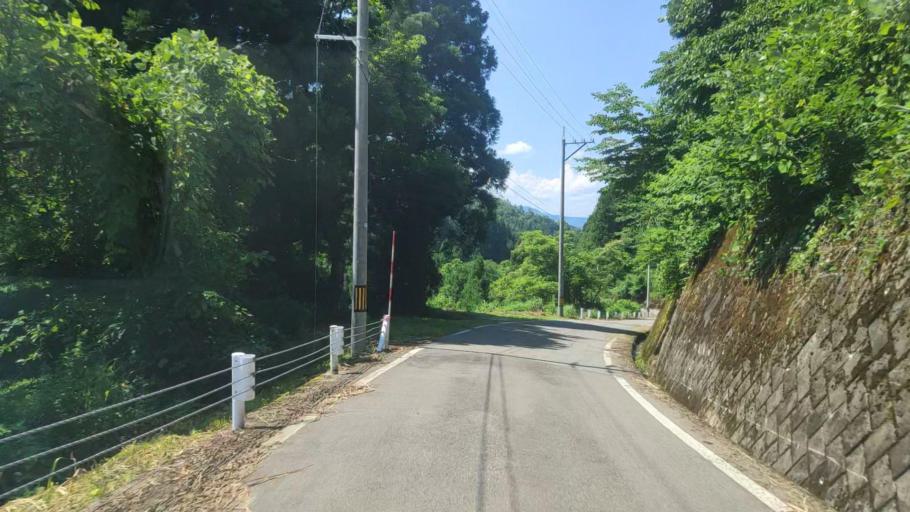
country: JP
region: Fukui
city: Katsuyama
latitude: 36.1186
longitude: 136.5080
